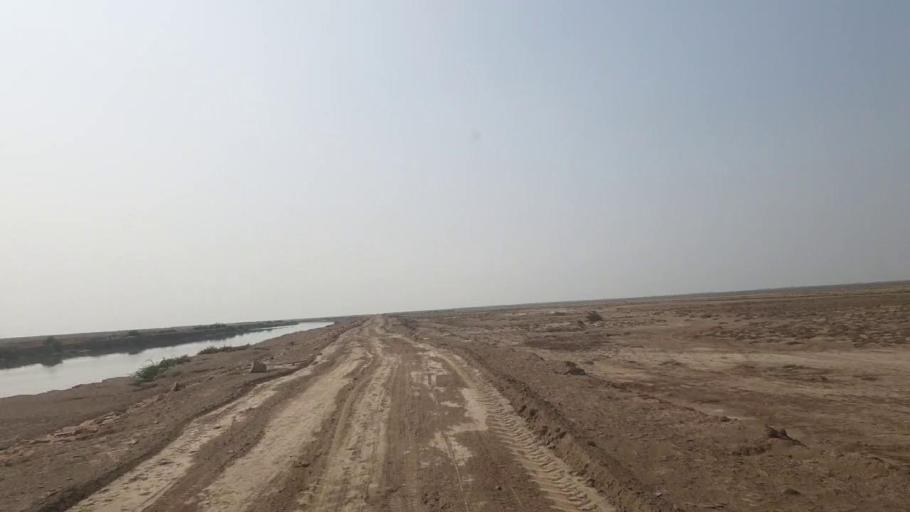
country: PK
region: Sindh
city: Kadhan
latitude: 24.3388
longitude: 68.8525
